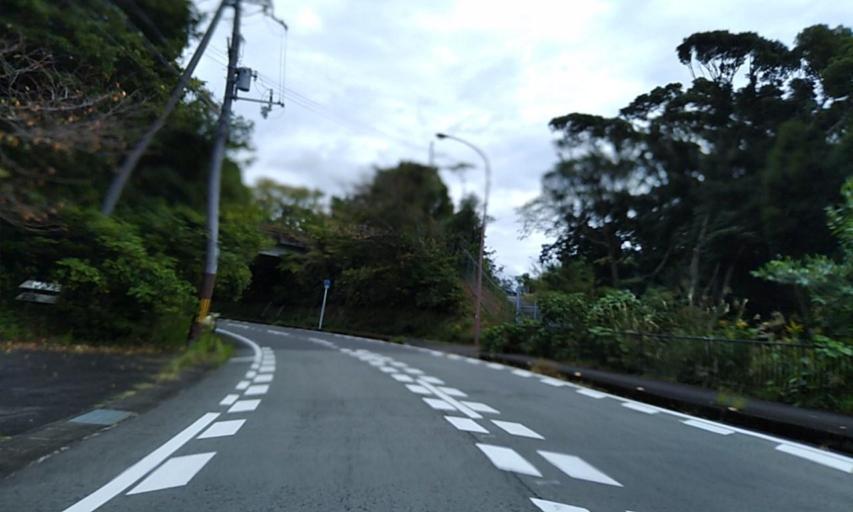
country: JP
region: Wakayama
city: Shingu
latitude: 33.4709
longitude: 135.8083
